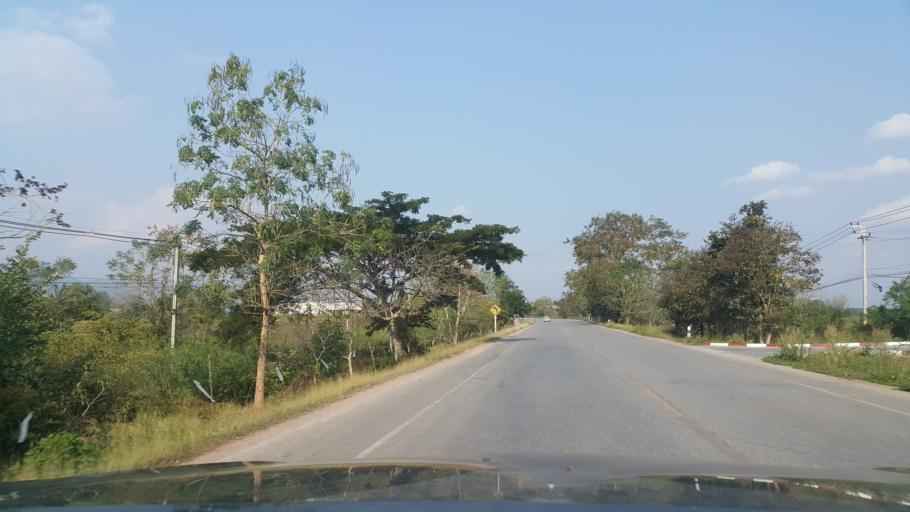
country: TH
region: Phitsanulok
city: Nakhon Thai
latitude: 17.0717
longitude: 100.8116
